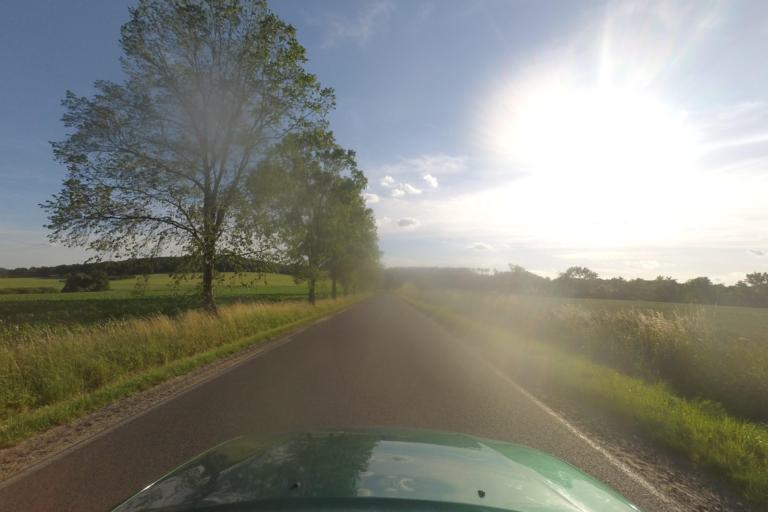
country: PL
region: Lower Silesian Voivodeship
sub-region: Powiat dzierzoniowski
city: Niemcza
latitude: 50.7166
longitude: 16.8055
